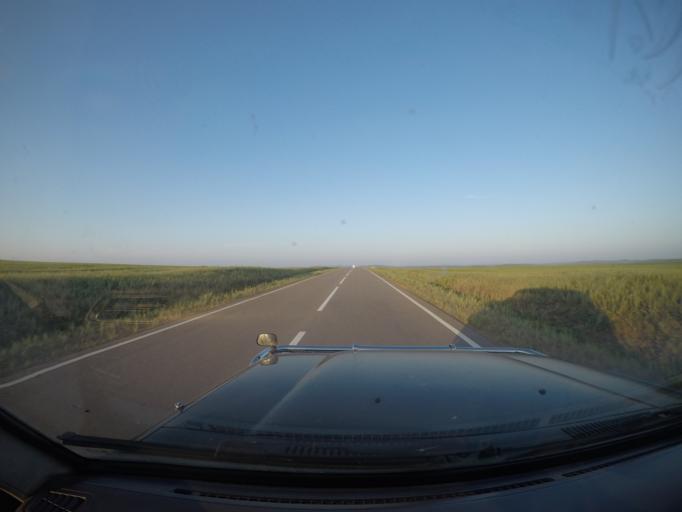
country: MN
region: Suhbaatar
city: Hanhohiy
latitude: 47.5700
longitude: 112.2994
